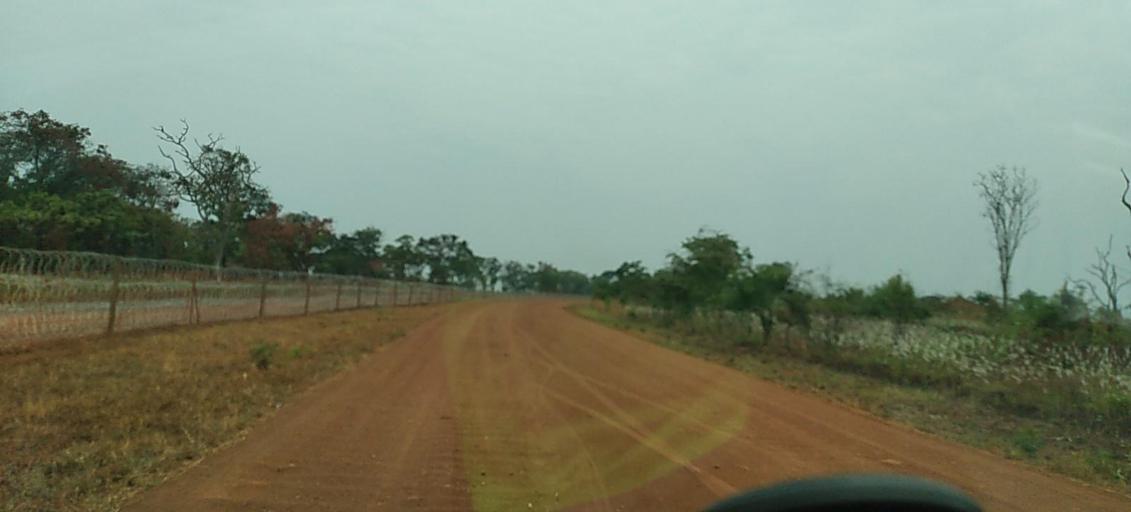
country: ZM
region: North-Western
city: Kansanshi
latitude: -12.0908
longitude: 26.4872
